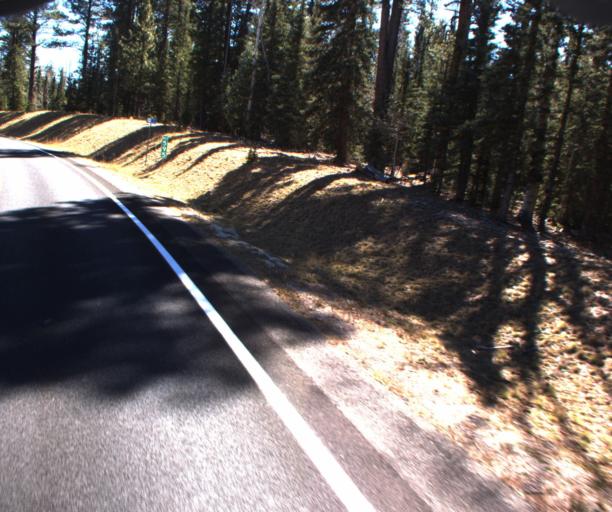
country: US
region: Arizona
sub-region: Coconino County
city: Grand Canyon
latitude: 36.5352
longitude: -112.1573
